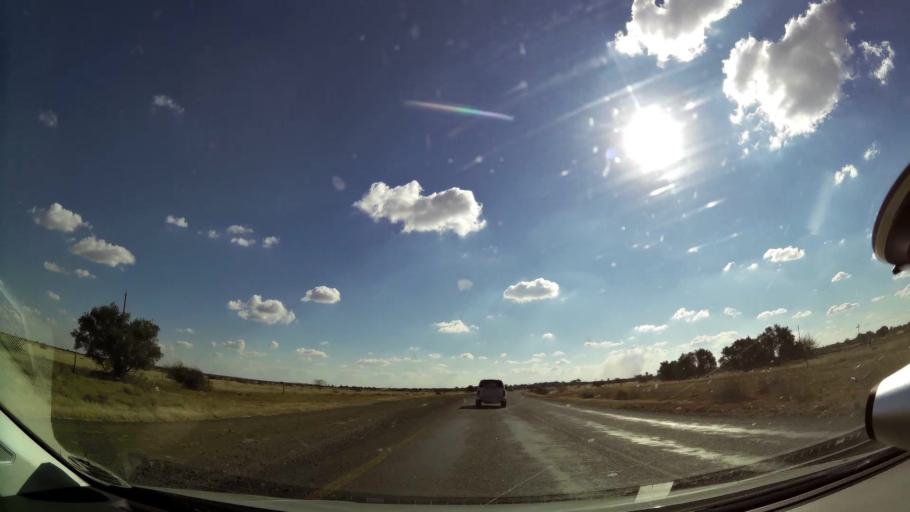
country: ZA
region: Northern Cape
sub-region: Frances Baard District Municipality
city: Kimberley
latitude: -28.8040
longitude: 24.7979
